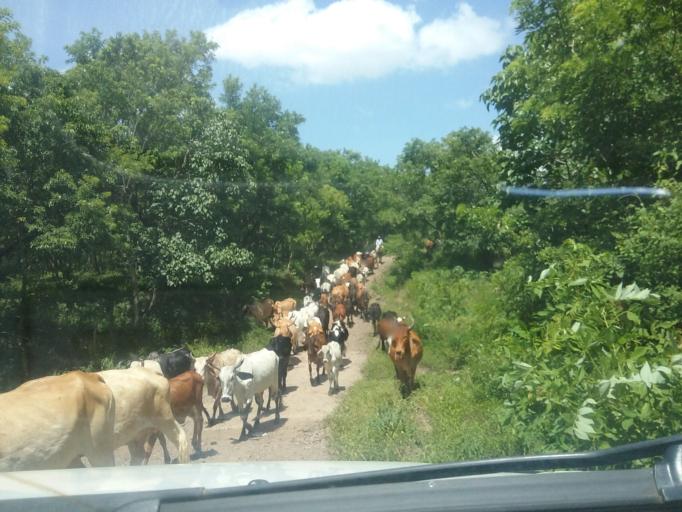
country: NI
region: Matagalpa
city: Terrabona
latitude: 12.6792
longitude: -85.9581
